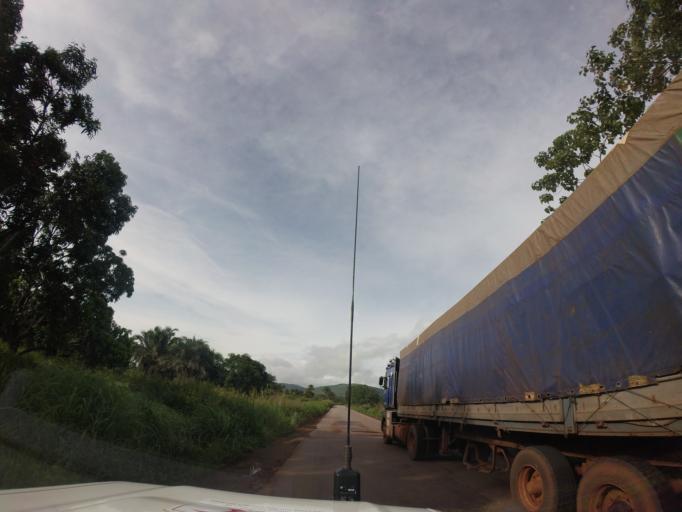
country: GN
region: Kindia
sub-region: Kindia
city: Kindia
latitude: 9.8714
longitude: -13.0538
